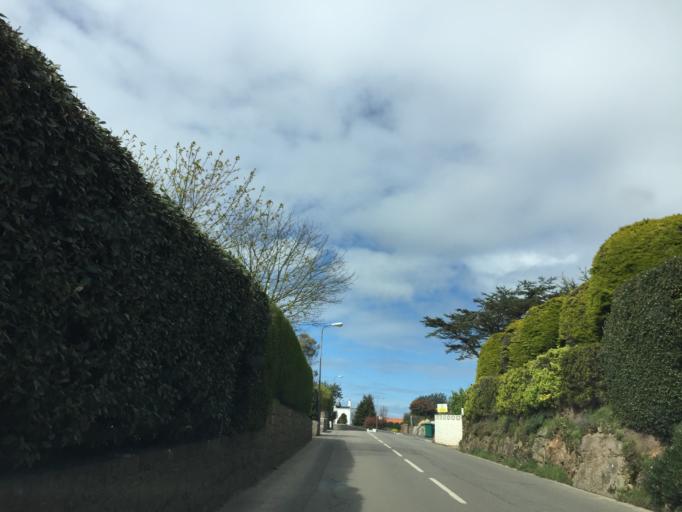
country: JE
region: St Helier
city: Saint Helier
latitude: 49.1799
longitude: -2.1755
